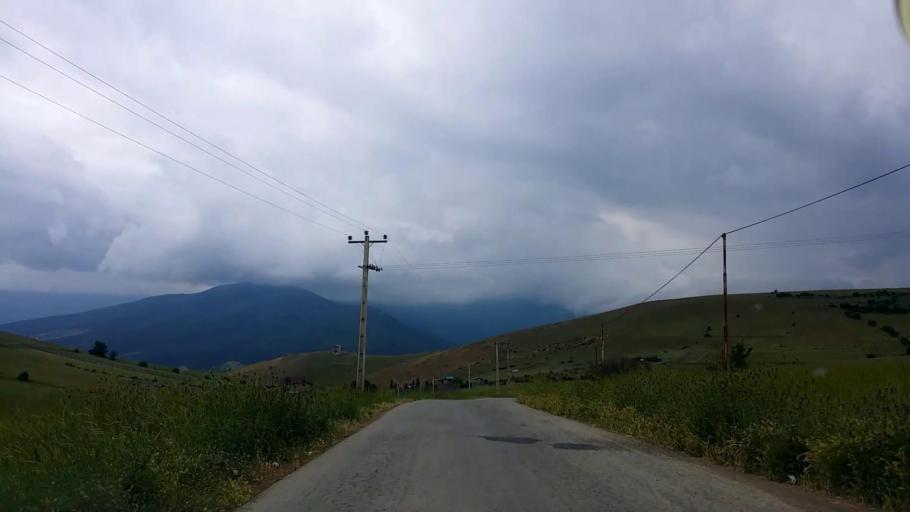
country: IR
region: Mazandaran
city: Chalus
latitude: 36.5260
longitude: 51.2658
